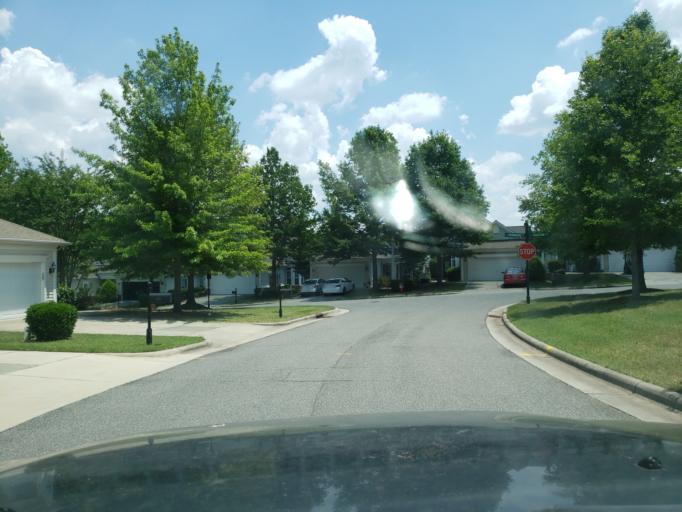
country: US
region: North Carolina
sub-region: Wake County
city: Green Level
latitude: 35.8330
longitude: -78.9143
